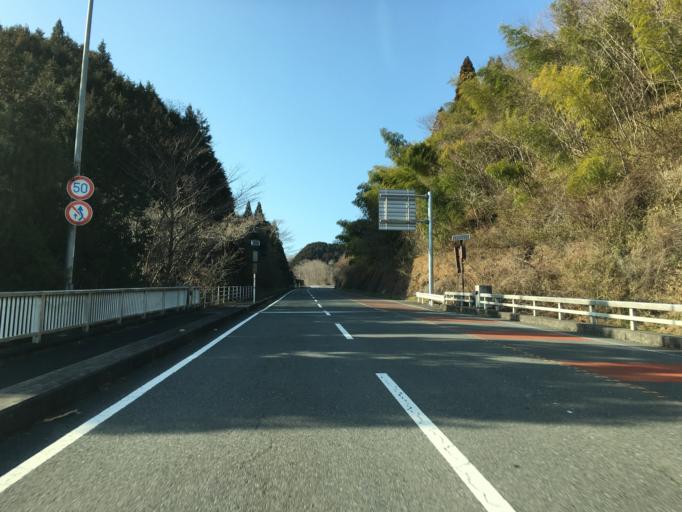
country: JP
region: Ibaraki
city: Takahagi
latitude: 36.7288
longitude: 140.6249
